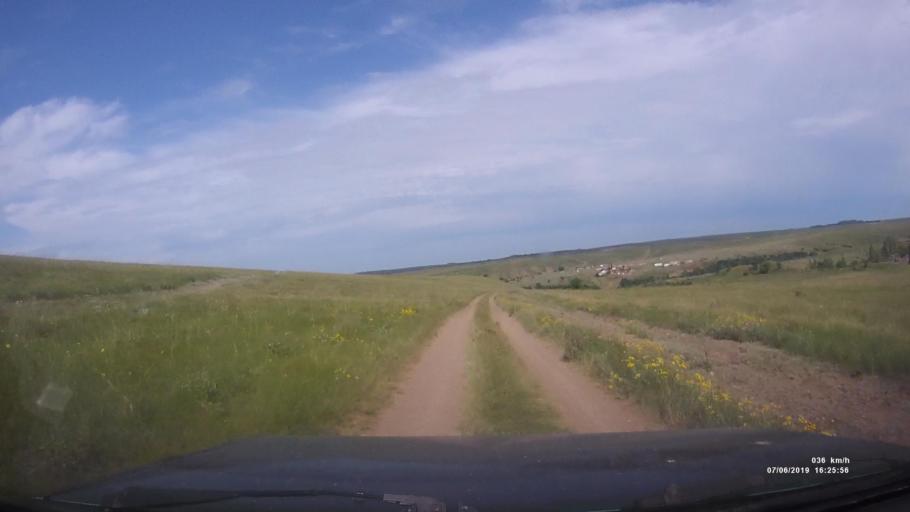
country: RU
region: Rostov
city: Kamensk-Shakhtinskiy
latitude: 48.2535
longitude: 40.3096
